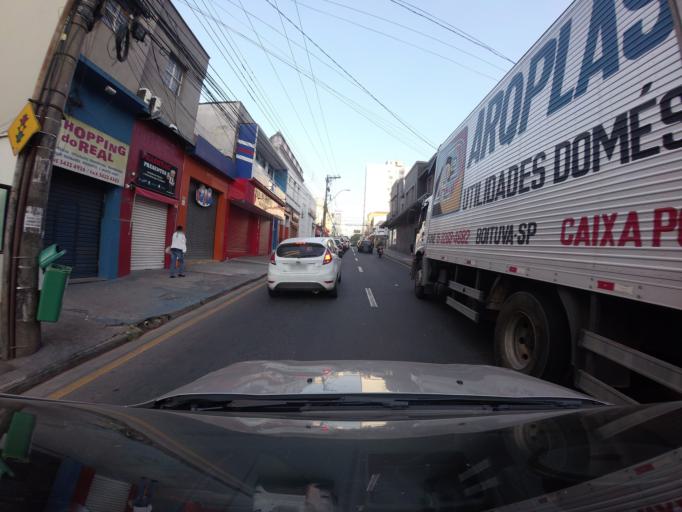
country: BR
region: Sao Paulo
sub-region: Piracicaba
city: Piracicaba
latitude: -22.7269
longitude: -47.6480
